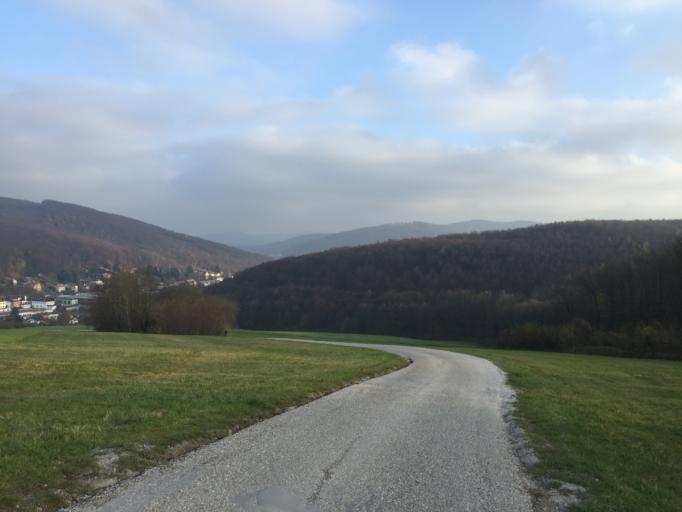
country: AT
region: Lower Austria
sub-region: Politischer Bezirk Wien-Umgebung
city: Gablitz
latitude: 48.2184
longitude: 16.1574
